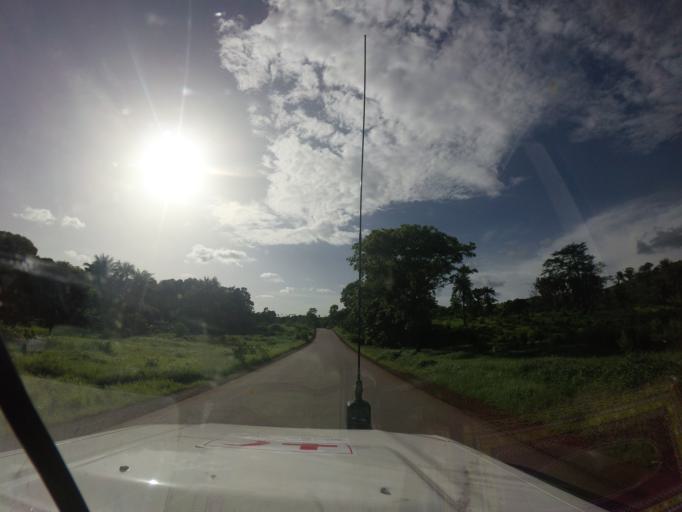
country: GN
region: Kindia
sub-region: Kindia
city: Kindia
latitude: 10.0924
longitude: -12.6175
